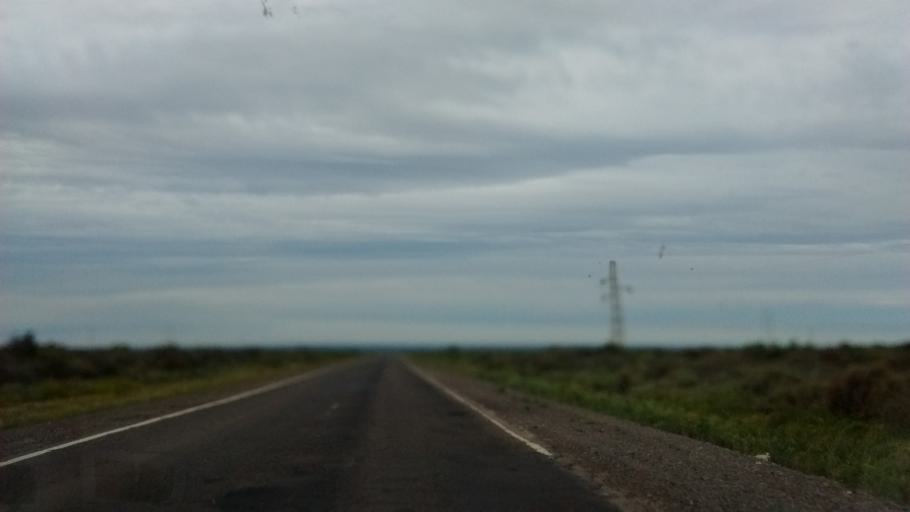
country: AR
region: Rio Negro
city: Catriel
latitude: -37.9717
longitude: -67.9029
